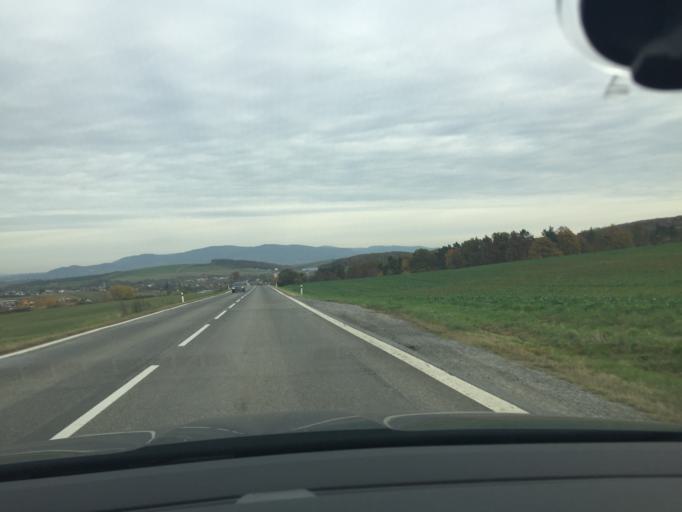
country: SK
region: Presovsky
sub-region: Okres Presov
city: Presov
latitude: 49.0069
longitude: 21.1541
